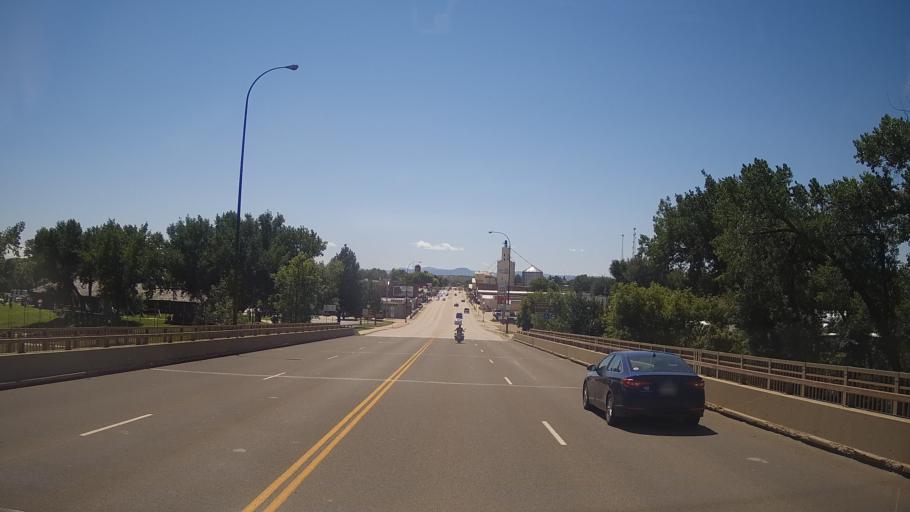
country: US
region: South Dakota
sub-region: Butte County
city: Belle Fourche
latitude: 44.6754
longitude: -103.8536
